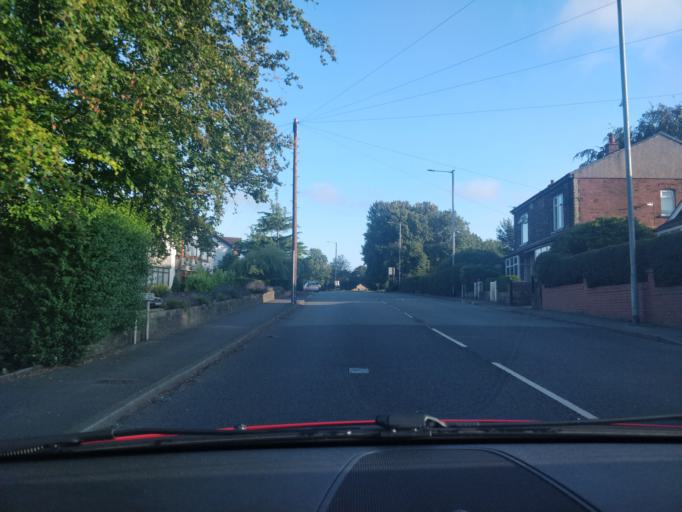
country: GB
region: England
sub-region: Lancashire
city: Appley Bridge
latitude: 53.5463
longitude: -2.7266
